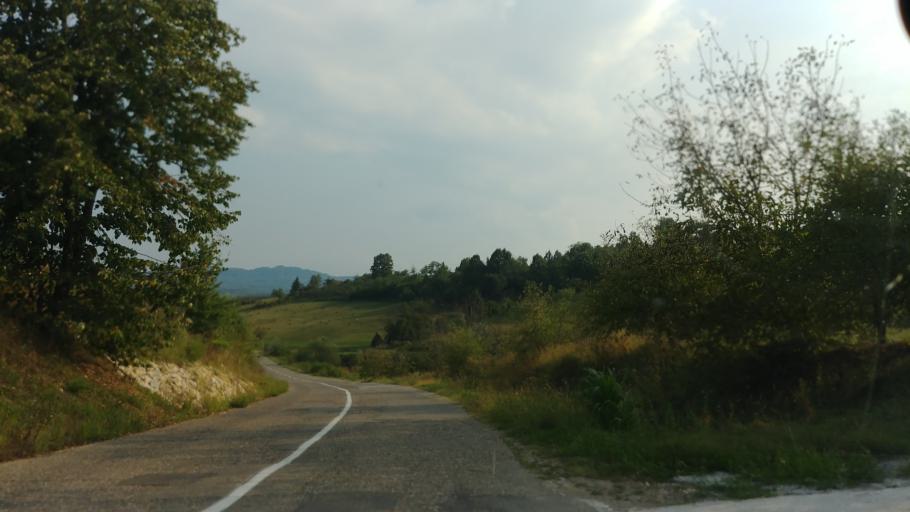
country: BA
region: Republika Srpska
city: Lopare
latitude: 44.7285
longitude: 18.8811
